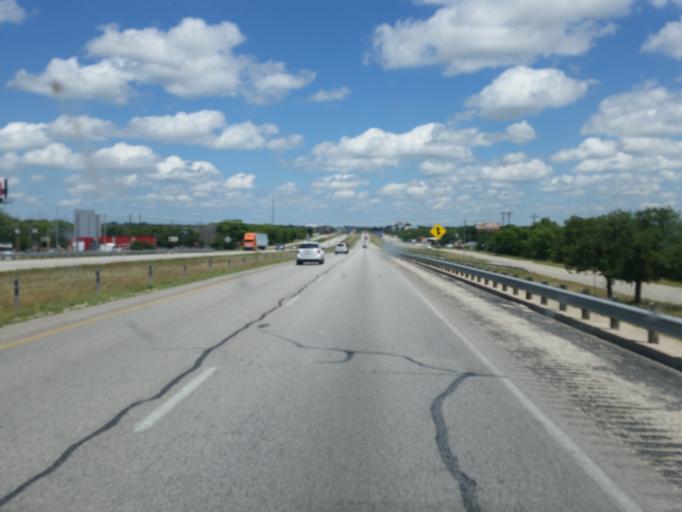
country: US
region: Texas
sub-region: Callahan County
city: Clyde
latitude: 32.4149
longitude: -99.5071
